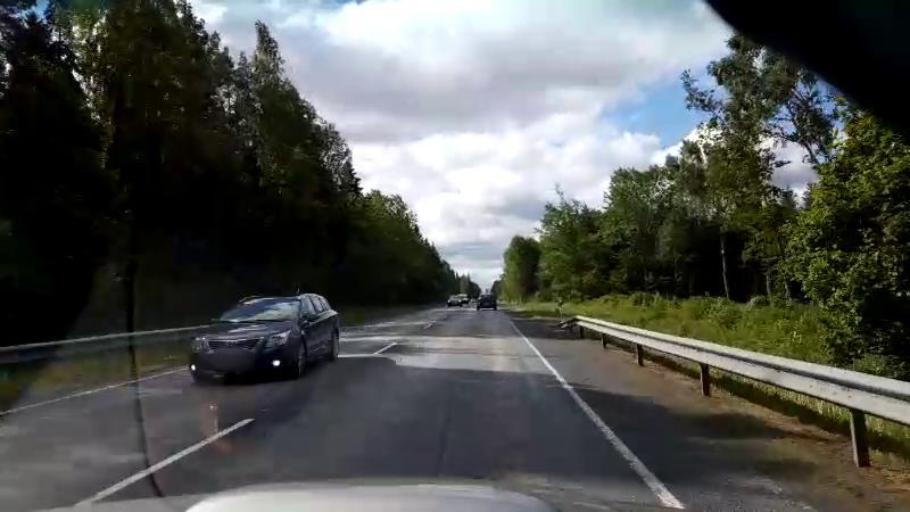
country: EE
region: Harju
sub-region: Saue linn
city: Saue
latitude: 59.2151
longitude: 24.4956
